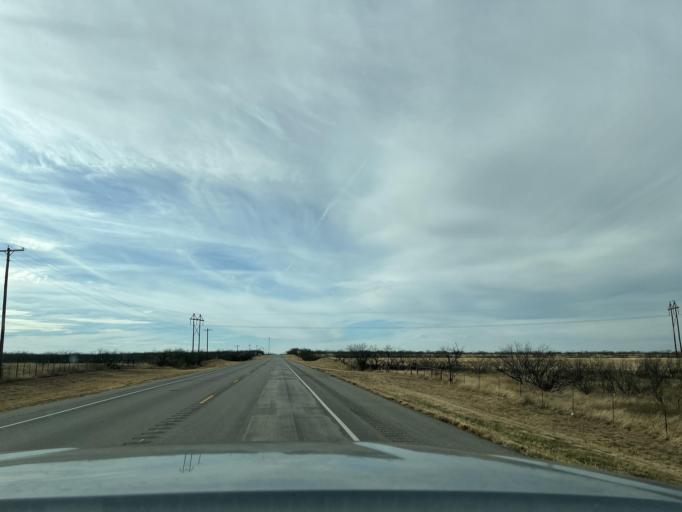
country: US
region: Texas
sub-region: Jones County
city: Anson
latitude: 32.7508
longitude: -99.7060
